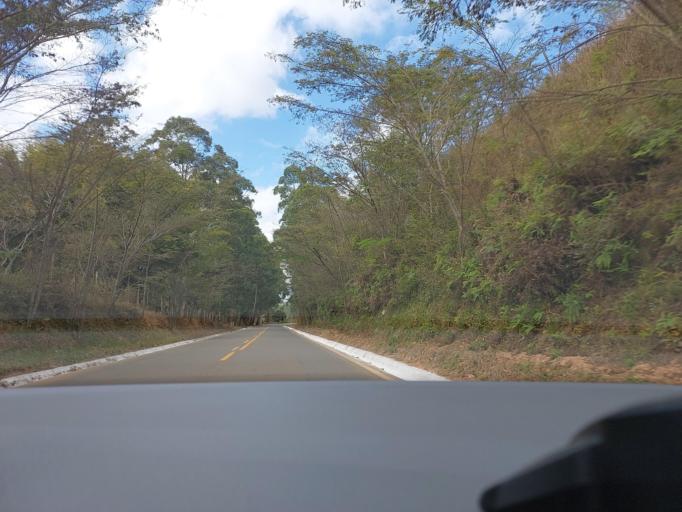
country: BR
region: Minas Gerais
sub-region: Visconde Do Rio Branco
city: Visconde do Rio Branco
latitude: -20.9067
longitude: -42.6480
